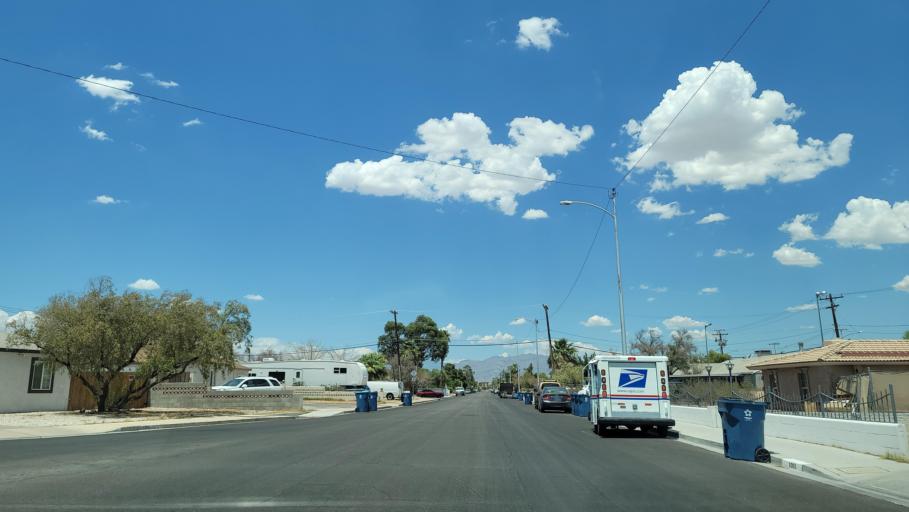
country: US
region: Nevada
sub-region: Clark County
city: Las Vegas
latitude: 36.1601
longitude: -115.1973
